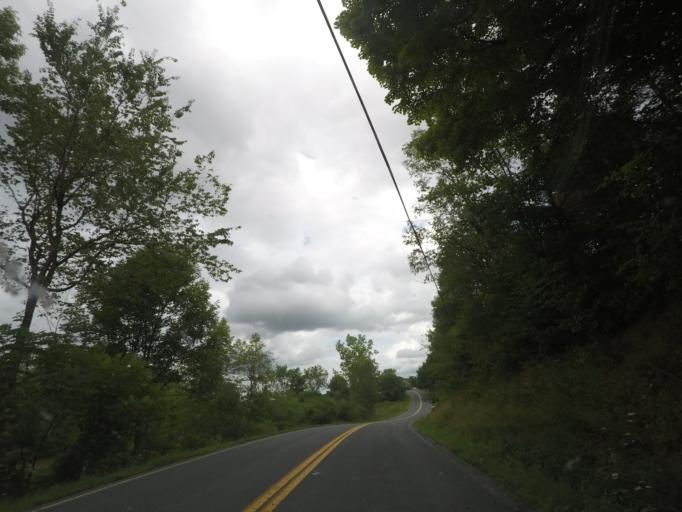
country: US
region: New York
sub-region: Rensselaer County
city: Wynantskill
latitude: 42.6742
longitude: -73.6386
